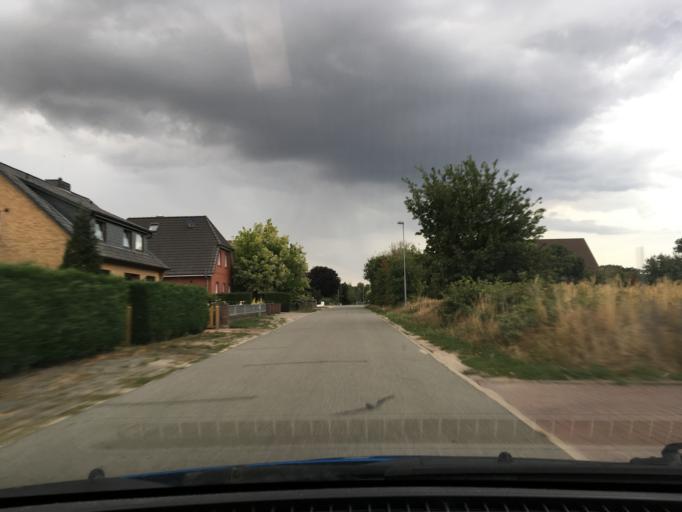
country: DE
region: Schleswig-Holstein
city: Lanze
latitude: 53.3895
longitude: 10.6070
